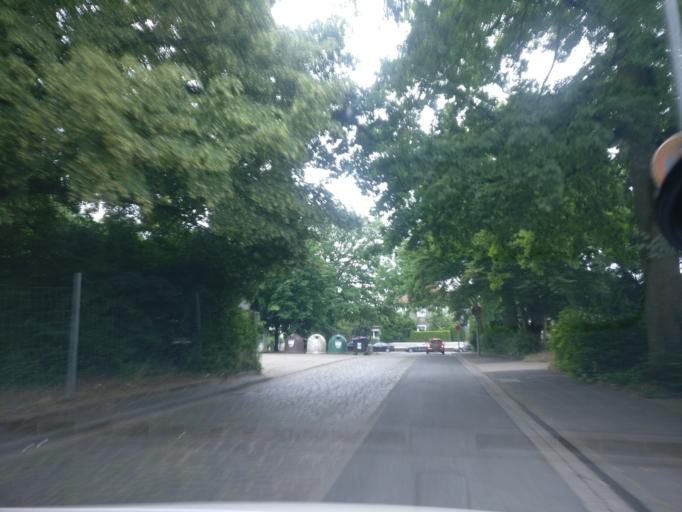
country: DE
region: Lower Saxony
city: Laatzen
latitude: 52.3619
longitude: 9.8325
